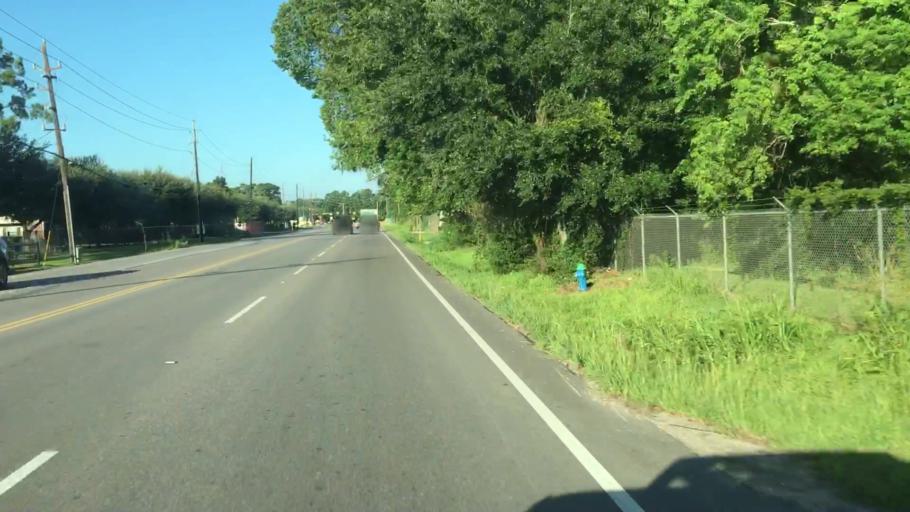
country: US
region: Texas
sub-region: Harris County
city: Humble
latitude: 29.9580
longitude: -95.2621
